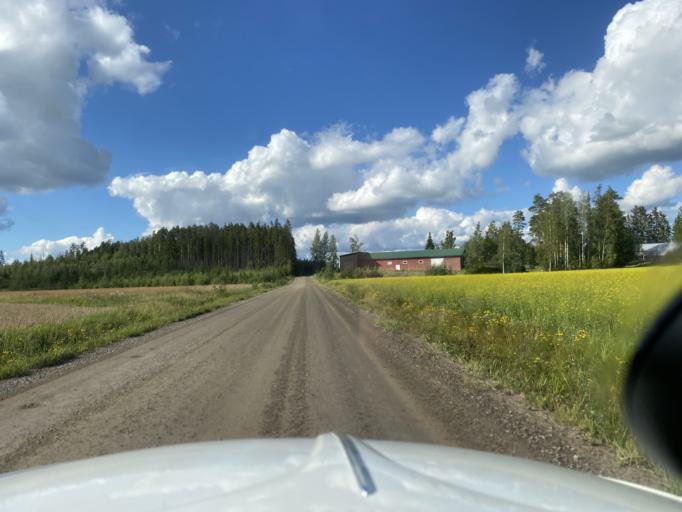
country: FI
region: Pirkanmaa
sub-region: Lounais-Pirkanmaa
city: Punkalaidun
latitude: 61.1139
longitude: 23.2739
